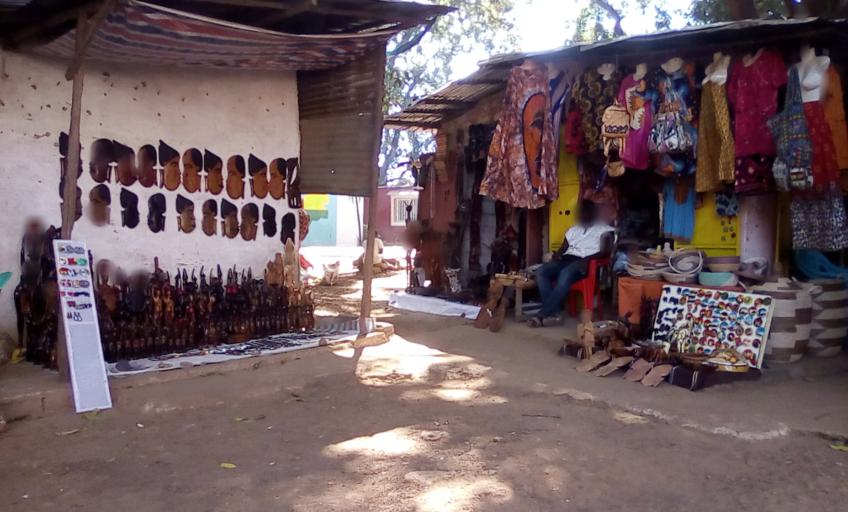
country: GW
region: Bissau
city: Bissau
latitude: 11.8662
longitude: -15.5858
